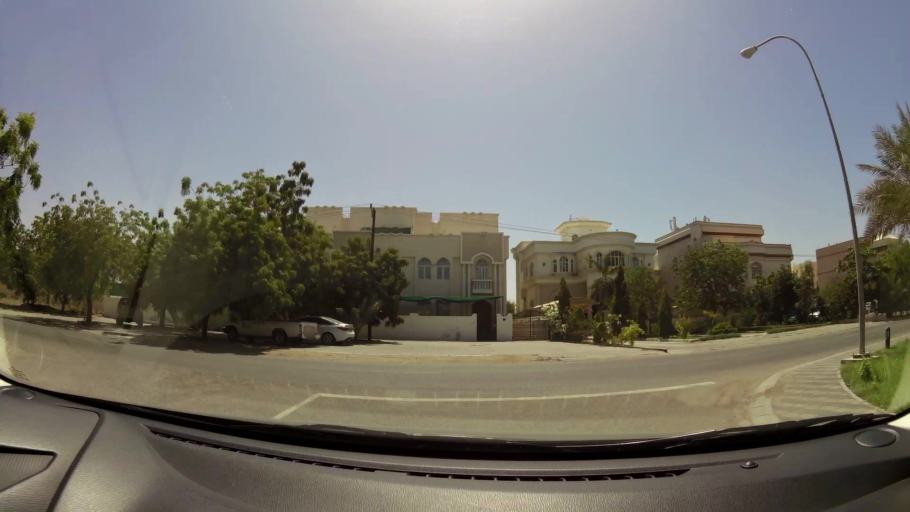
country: OM
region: Muhafazat Masqat
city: Bawshar
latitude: 23.5984
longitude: 58.3577
